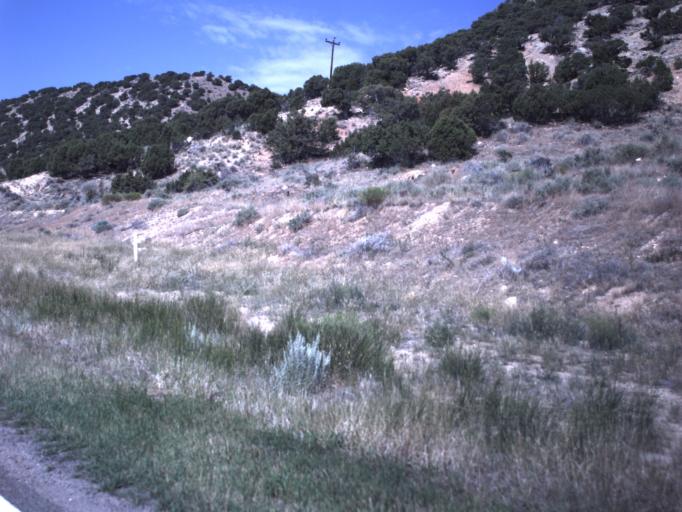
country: US
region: Utah
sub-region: Daggett County
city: Manila
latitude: 40.9838
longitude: -109.7389
